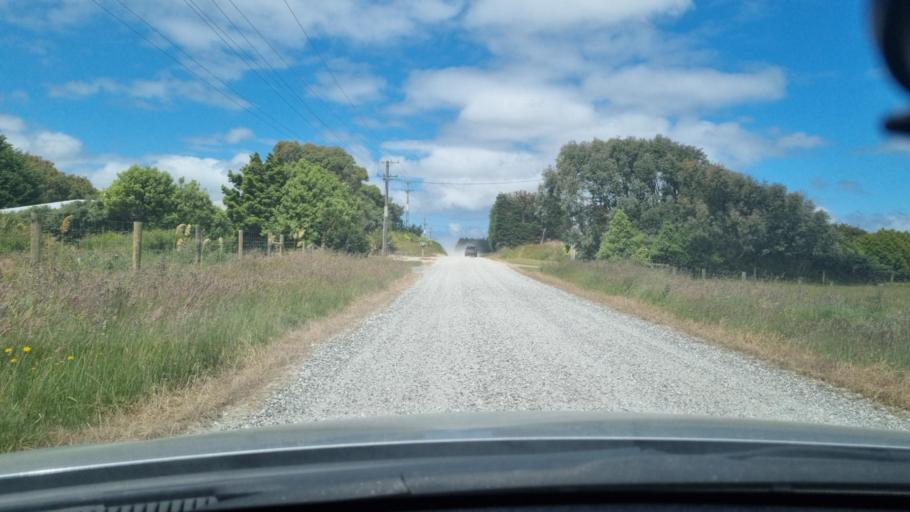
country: NZ
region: Southland
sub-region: Invercargill City
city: Invercargill
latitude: -46.4489
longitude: 168.3034
